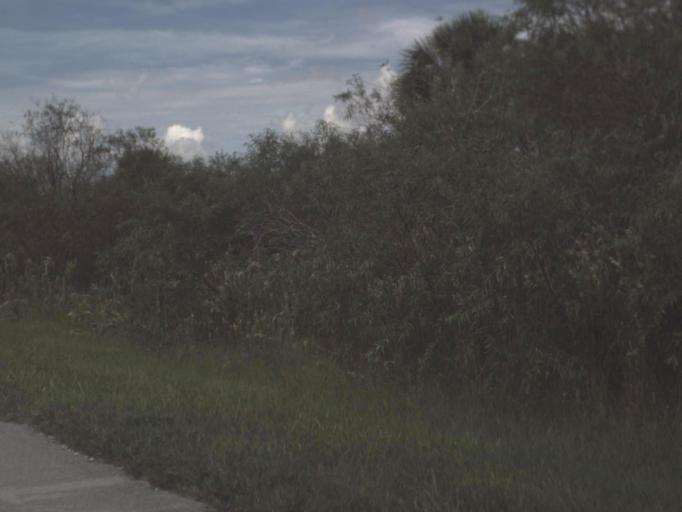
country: US
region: Florida
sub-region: Highlands County
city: Placid Lakes
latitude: 27.2090
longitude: -81.4383
